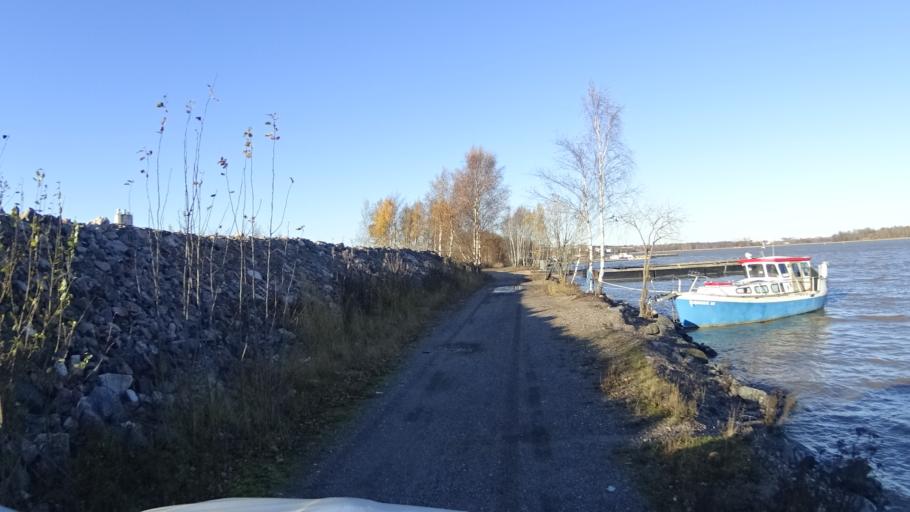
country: FI
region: Uusimaa
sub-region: Helsinki
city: Helsinki
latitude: 60.1933
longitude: 24.9853
